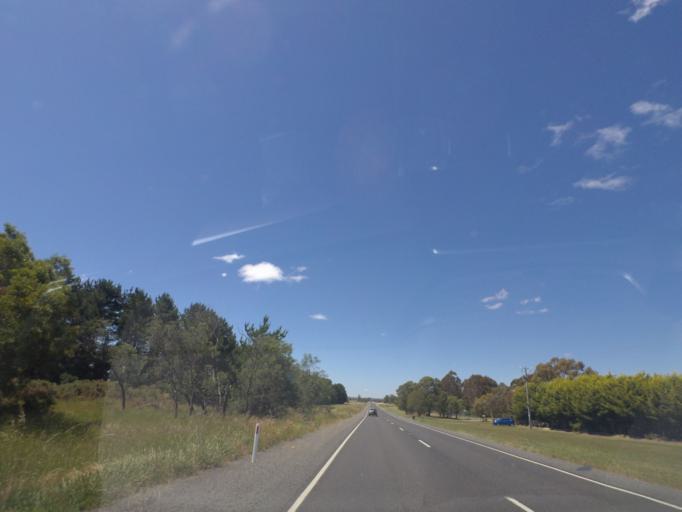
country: AU
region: Victoria
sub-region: Mount Alexander
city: Castlemaine
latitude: -37.2301
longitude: 144.3334
